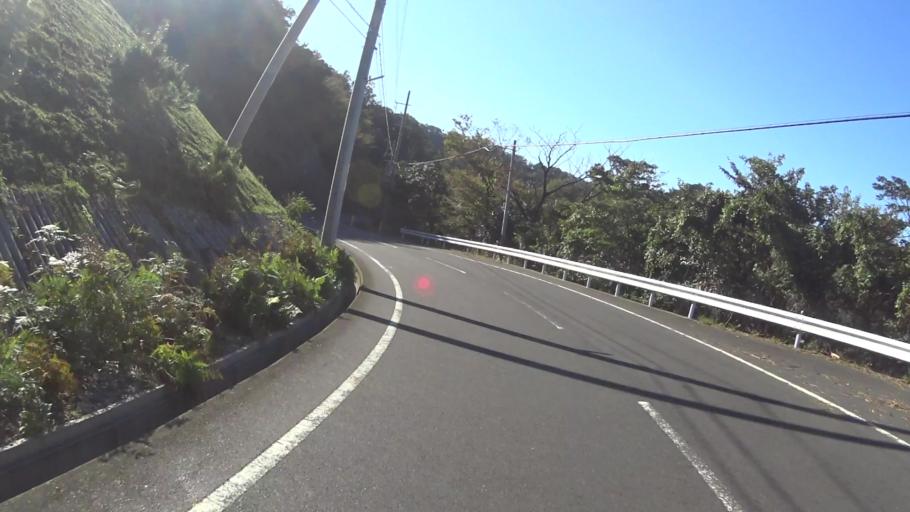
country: JP
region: Hyogo
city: Toyooka
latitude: 35.6438
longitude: 134.8872
